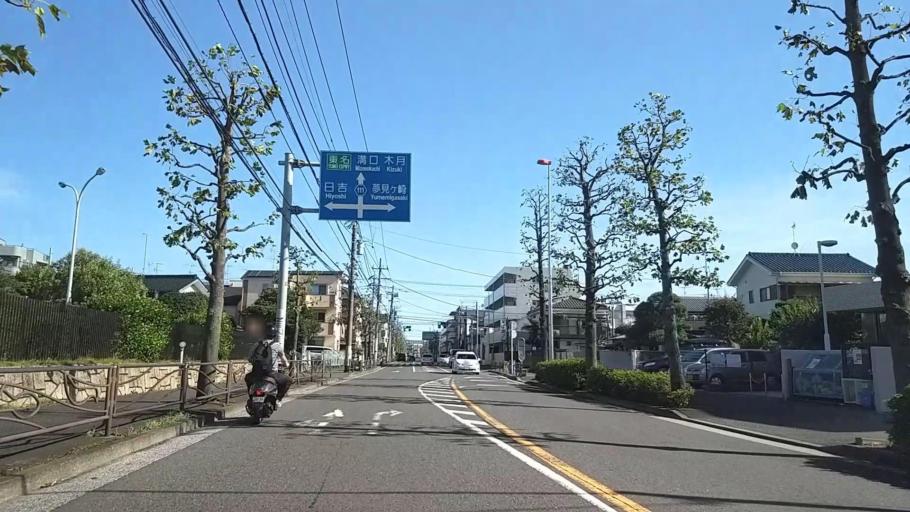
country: JP
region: Kanagawa
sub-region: Kawasaki-shi
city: Kawasaki
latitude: 35.5446
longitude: 139.6573
